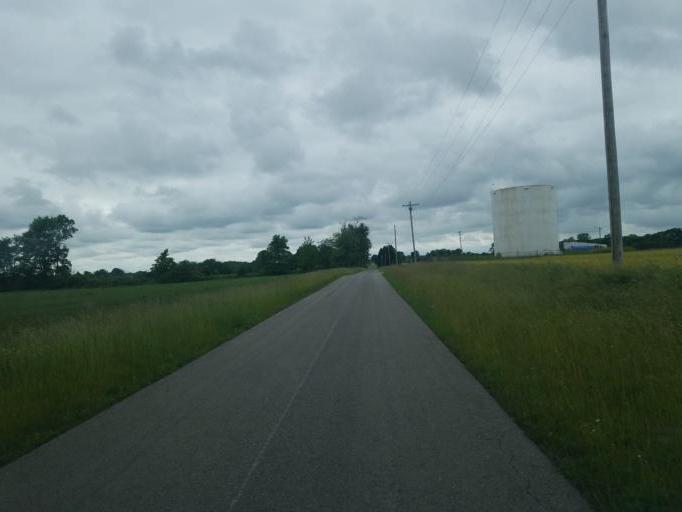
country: US
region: Ohio
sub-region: Morrow County
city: Cardington
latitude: 40.5684
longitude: -82.9056
